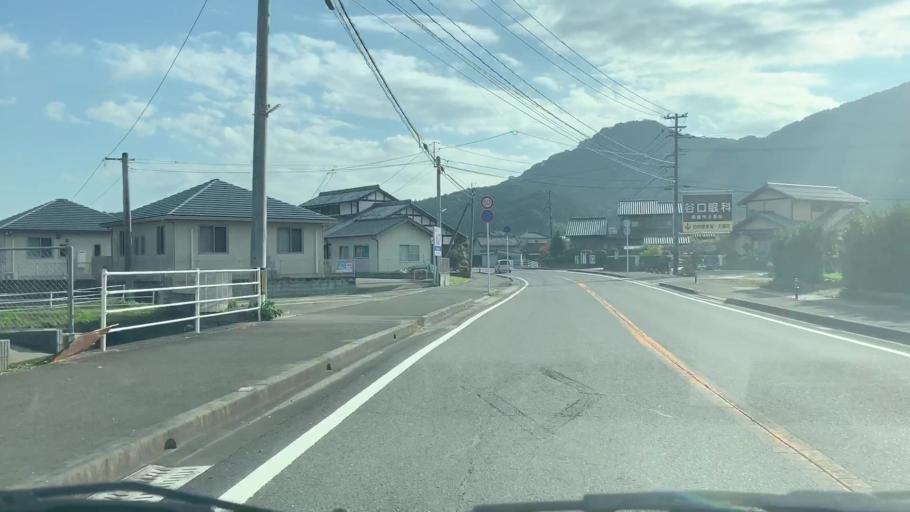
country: JP
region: Saga Prefecture
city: Takeocho-takeo
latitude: 33.1718
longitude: 130.0497
